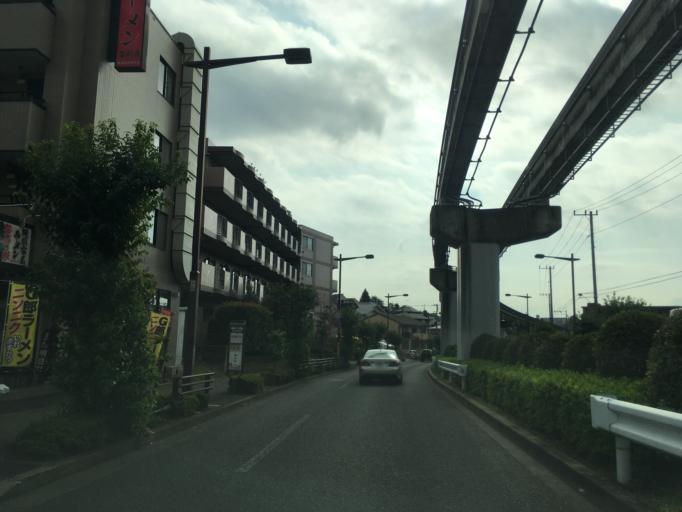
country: JP
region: Tokyo
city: Hino
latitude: 35.6404
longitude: 139.4123
